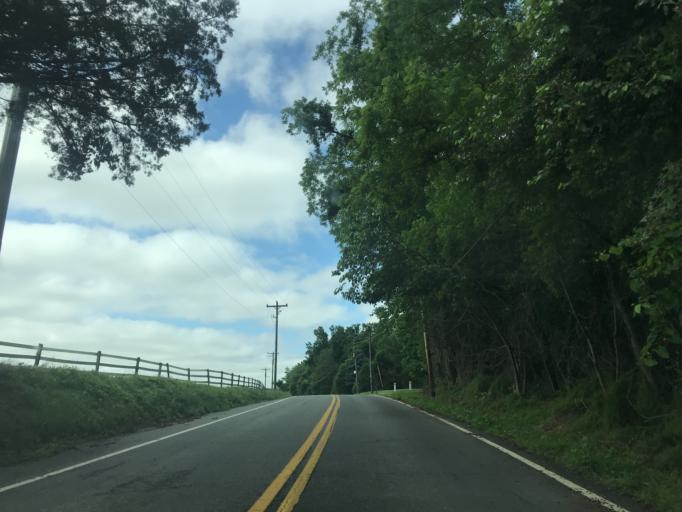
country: US
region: Maryland
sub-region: Caroline County
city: Ridgely
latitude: 38.8892
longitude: -75.9607
